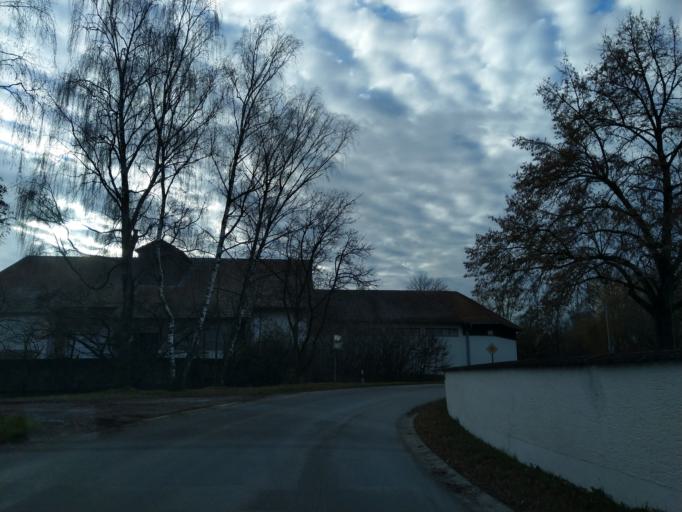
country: DE
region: Bavaria
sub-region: Lower Bavaria
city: Aholming
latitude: 48.7178
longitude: 12.9042
